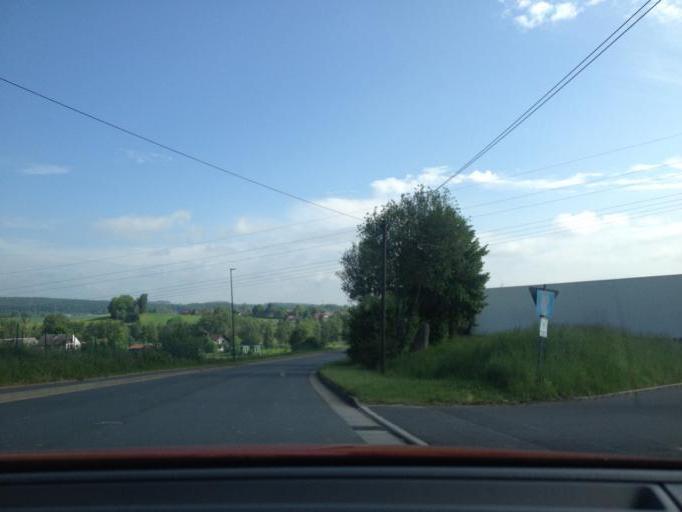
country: DE
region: Bavaria
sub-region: Upper Franconia
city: Marktredwitz
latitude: 50.0163
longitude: 12.0962
